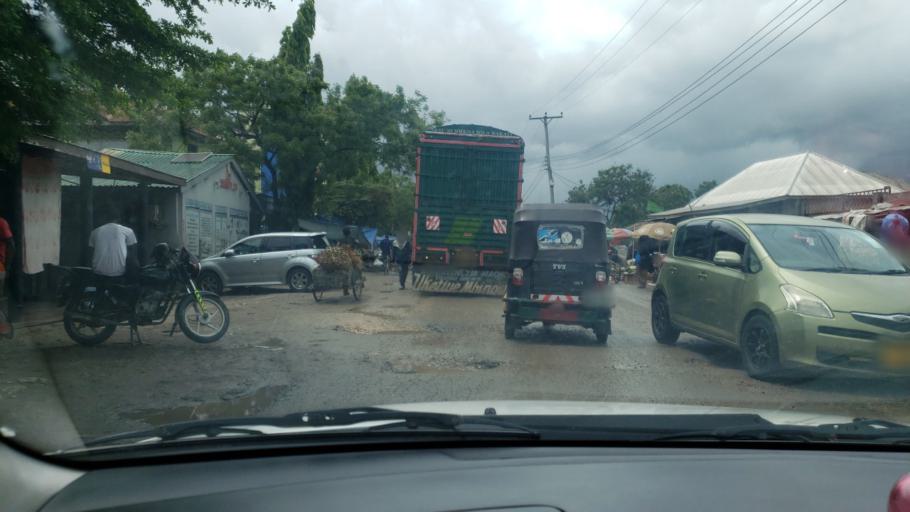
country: TZ
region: Dar es Salaam
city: Magomeni
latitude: -6.7989
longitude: 39.2255
